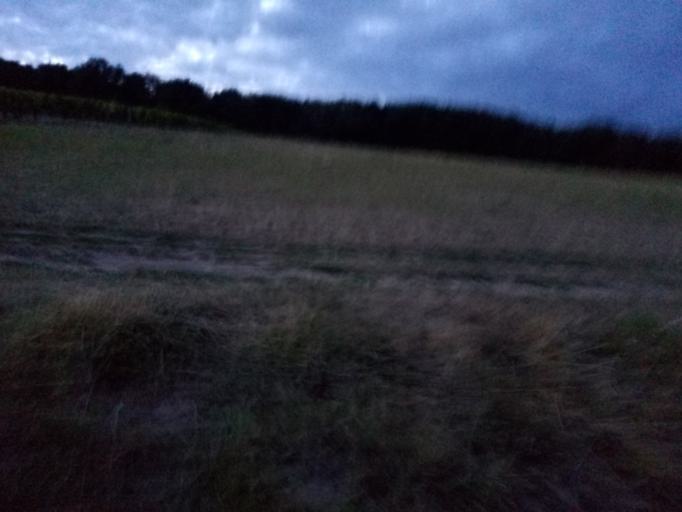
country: DE
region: Rheinland-Pfalz
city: Waldlaubersheim
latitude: 49.9377
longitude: 7.8302
